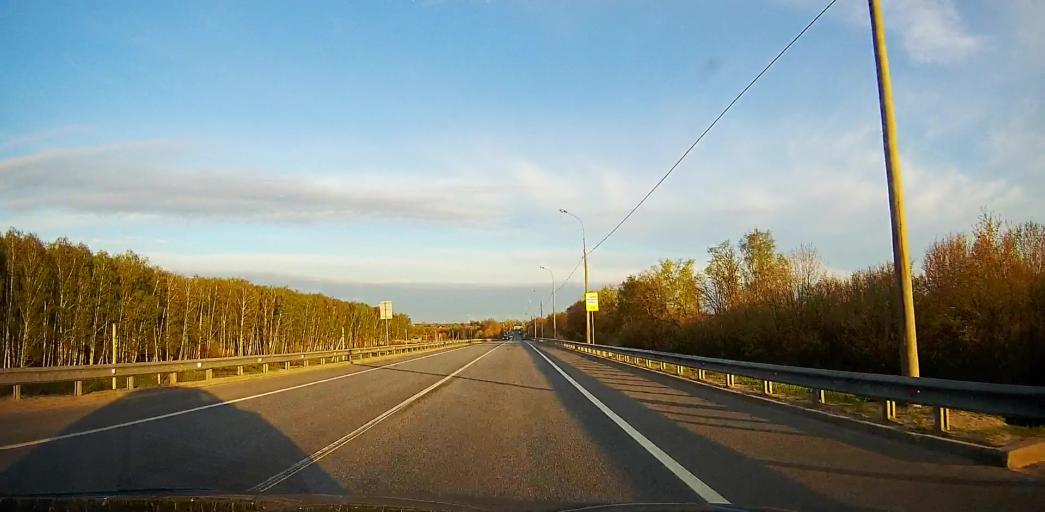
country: RU
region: Moskovskaya
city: Troitskoye
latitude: 55.2339
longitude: 38.5493
